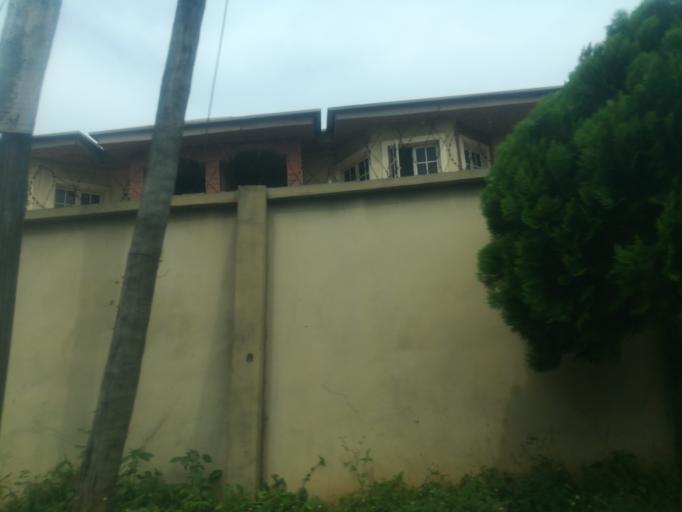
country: NG
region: Oyo
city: Ibadan
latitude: 7.4252
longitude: 3.9152
